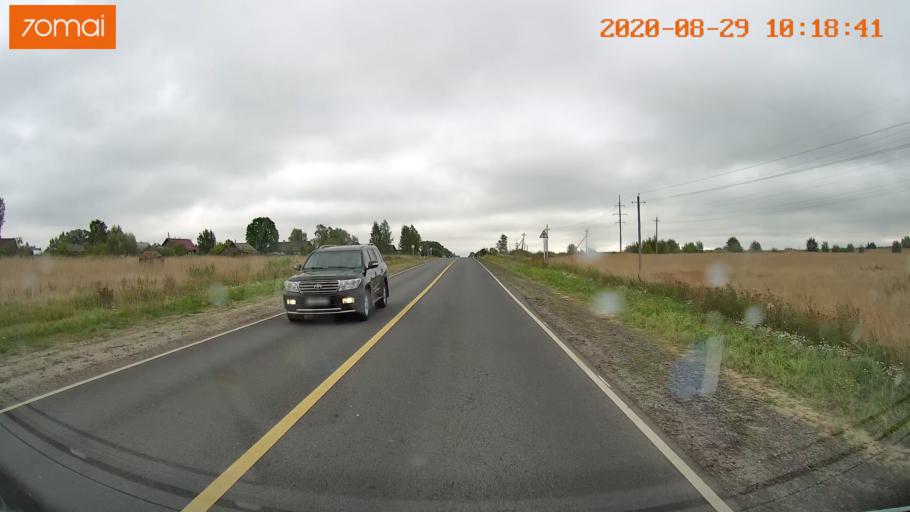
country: RU
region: Ivanovo
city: Yur'yevets
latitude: 57.3305
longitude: 42.8429
